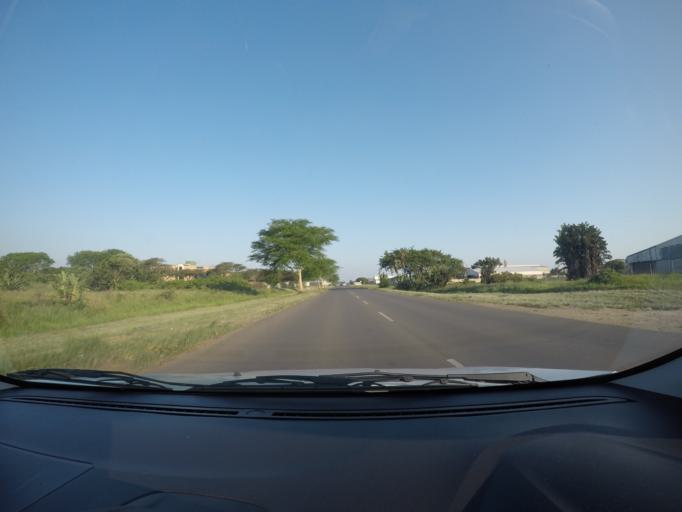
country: ZA
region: KwaZulu-Natal
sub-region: uThungulu District Municipality
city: Richards Bay
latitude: -28.7502
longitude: 32.0188
